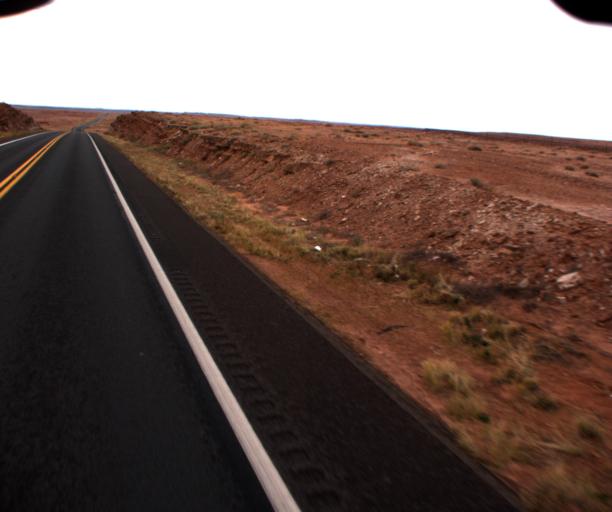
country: US
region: Arizona
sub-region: Coconino County
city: Tuba City
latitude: 36.1029
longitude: -111.2872
